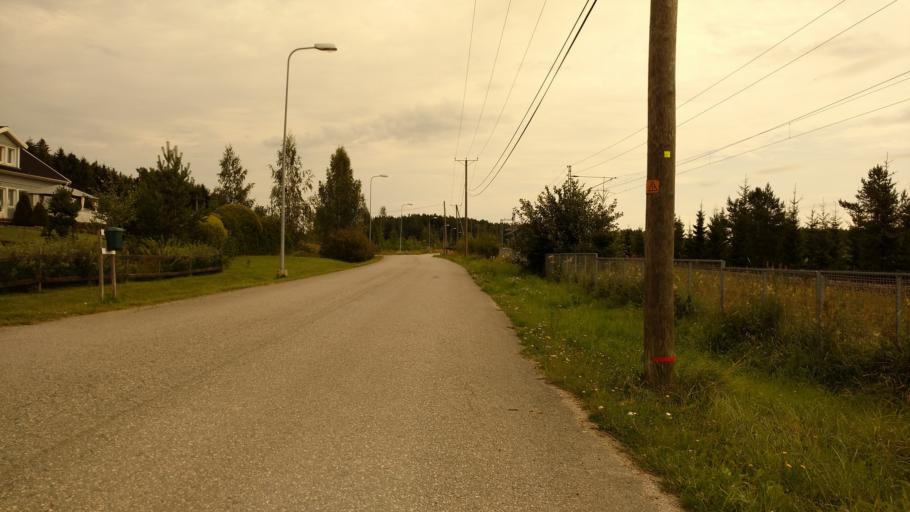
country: FI
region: Varsinais-Suomi
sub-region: Turku
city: Piikkioe
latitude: 60.4327
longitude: 22.5450
